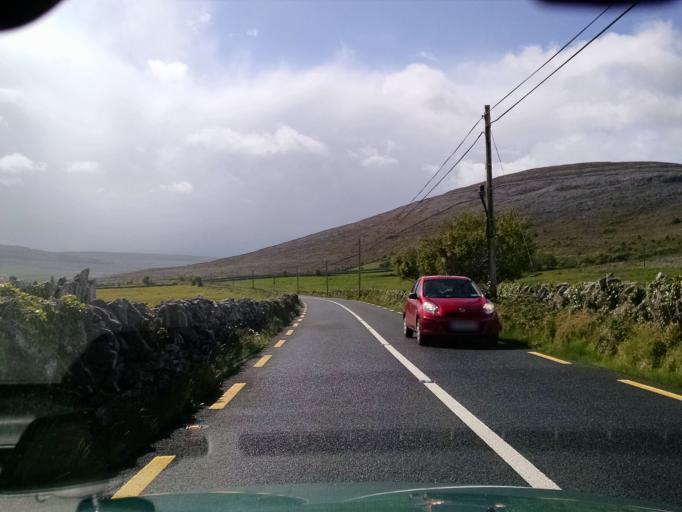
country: IE
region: Connaught
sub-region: County Galway
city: Bearna
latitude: 53.1321
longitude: -9.0969
